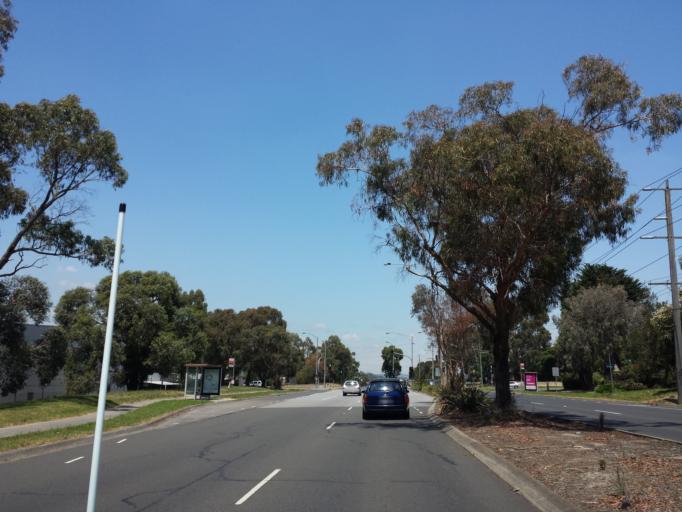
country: AU
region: Victoria
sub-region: Maroondah
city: Bayswater North
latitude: -37.8124
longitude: 145.2882
